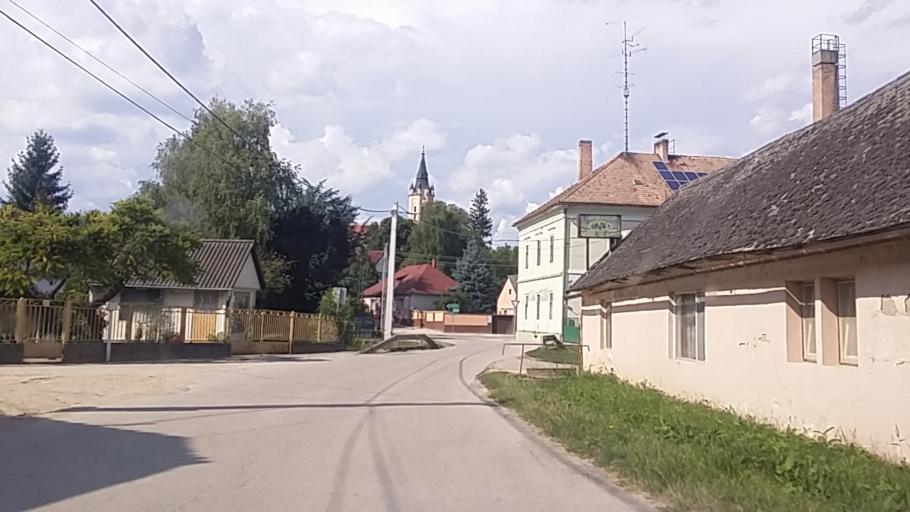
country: HU
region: Tolna
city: Gyonk
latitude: 46.5547
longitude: 18.4773
